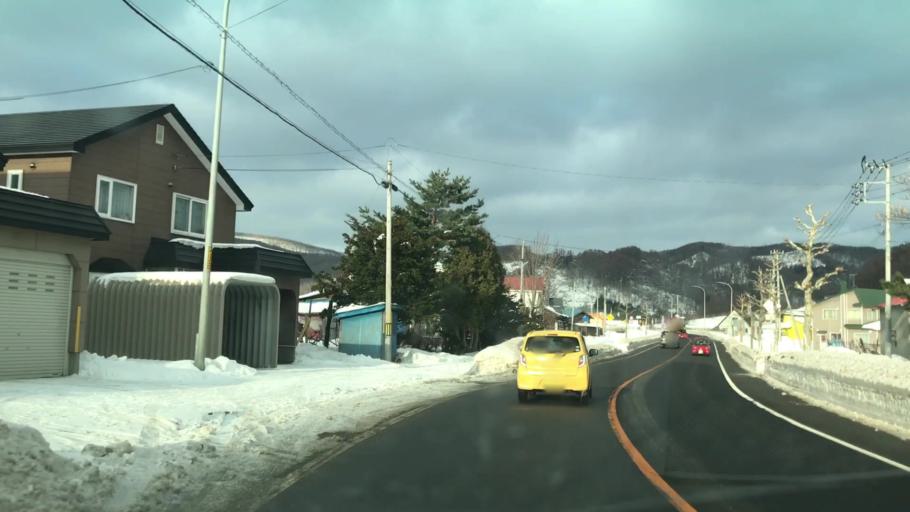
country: JP
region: Hokkaido
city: Yoichi
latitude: 43.2081
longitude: 140.7665
